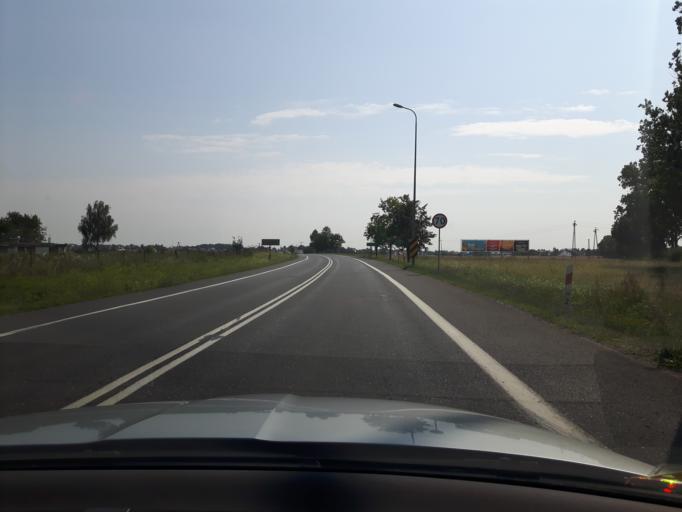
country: PL
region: Masovian Voivodeship
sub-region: Powiat mlawski
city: Mlawa
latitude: 53.1276
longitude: 20.3934
